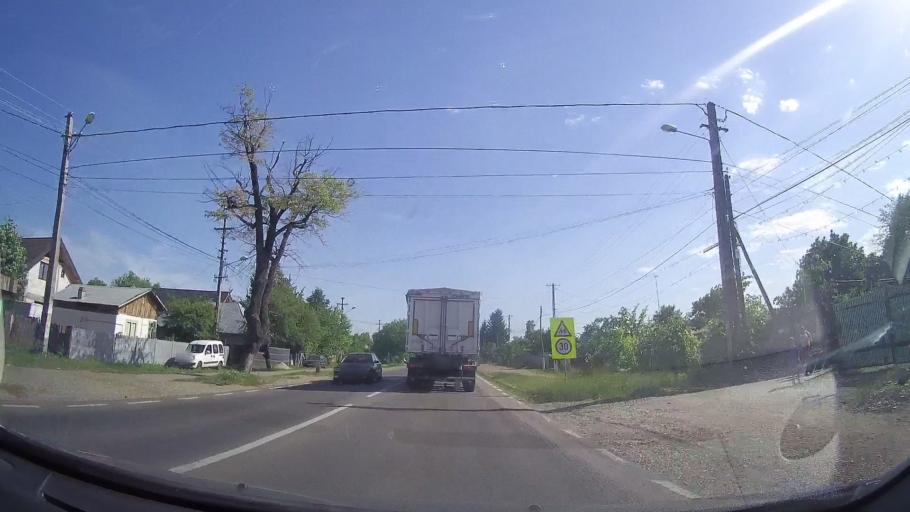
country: RO
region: Prahova
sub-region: Comuna Lipanesti
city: Lipanesti
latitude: 45.0485
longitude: 26.0191
